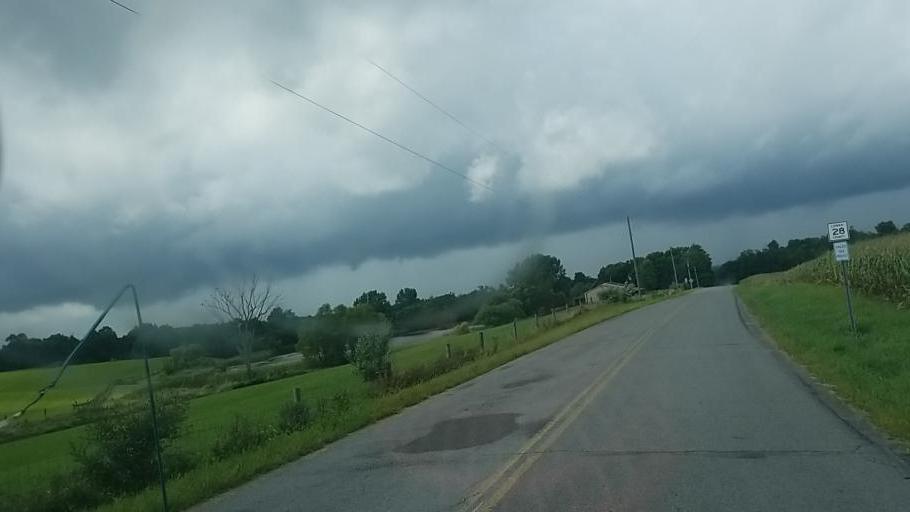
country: US
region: Ohio
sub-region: Champaign County
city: North Lewisburg
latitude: 40.2524
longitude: -83.6540
